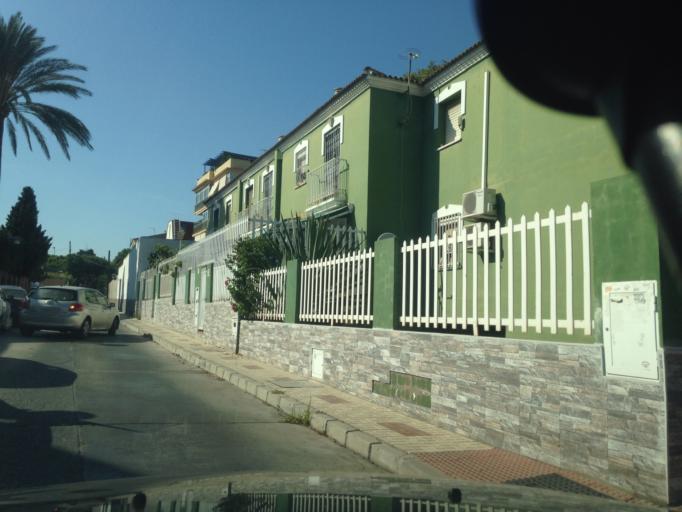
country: ES
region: Andalusia
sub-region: Provincia de Malaga
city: Malaga
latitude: 36.7234
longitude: -4.4555
